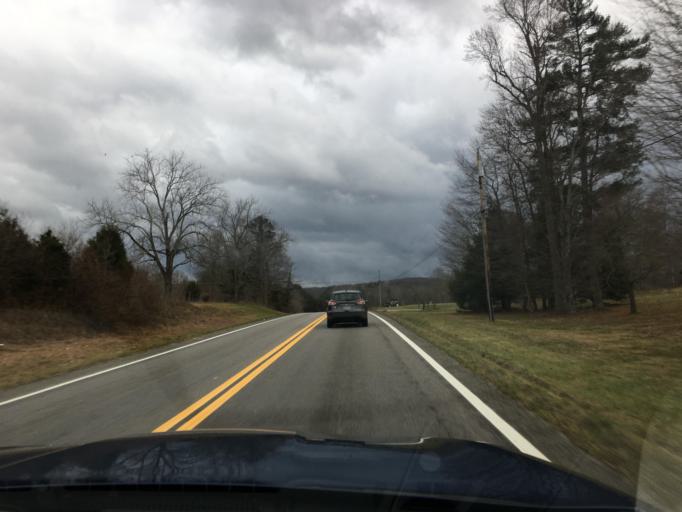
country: US
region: Tennessee
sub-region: Cumberland County
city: Crossville
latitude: 35.8841
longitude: -84.9368
